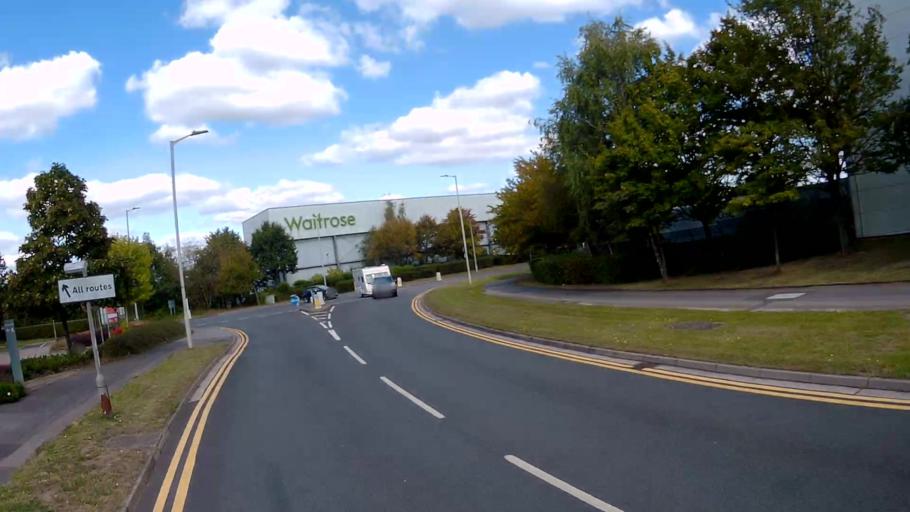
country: GB
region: England
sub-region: Bracknell Forest
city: Bracknell
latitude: 51.4112
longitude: -0.7738
